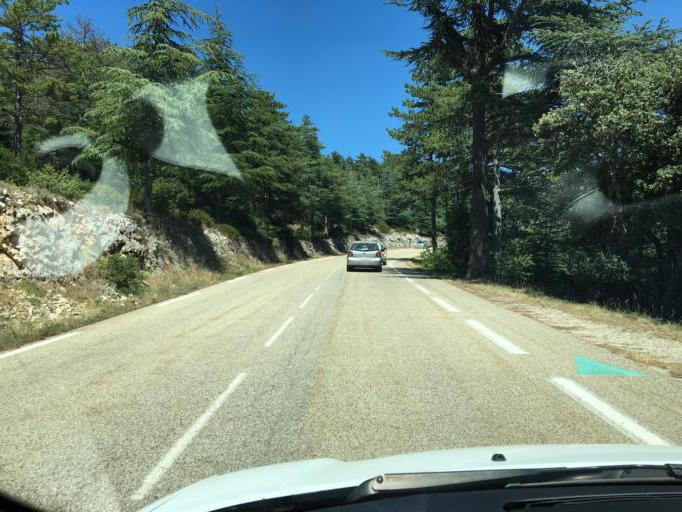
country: FR
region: Provence-Alpes-Cote d'Azur
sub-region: Departement du Vaucluse
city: Malaucene
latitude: 44.1652
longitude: 5.1626
